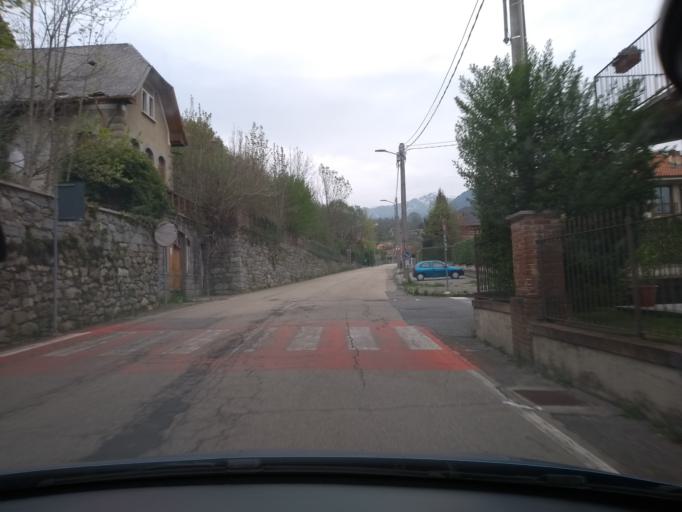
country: IT
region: Piedmont
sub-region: Provincia di Torino
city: Lanzo Torinese
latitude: 45.2771
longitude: 7.4711
